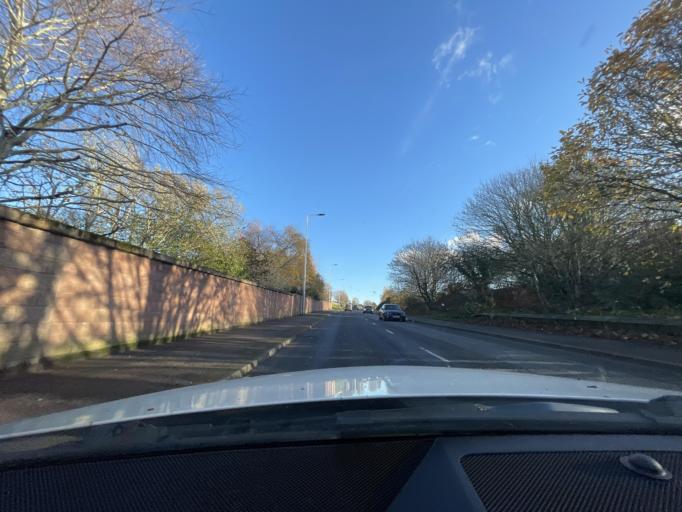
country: GB
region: Scotland
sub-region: Highland
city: Inverness
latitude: 57.4494
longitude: -4.2465
